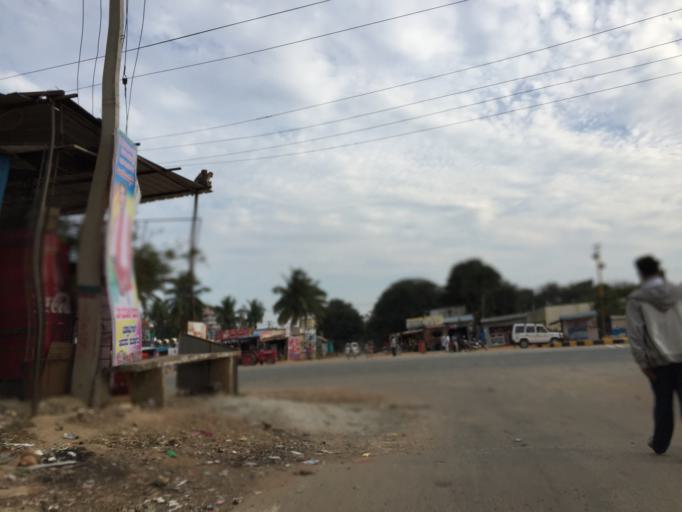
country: IN
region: Karnataka
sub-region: Kolar
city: Mulbagal
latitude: 13.1544
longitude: 78.3306
